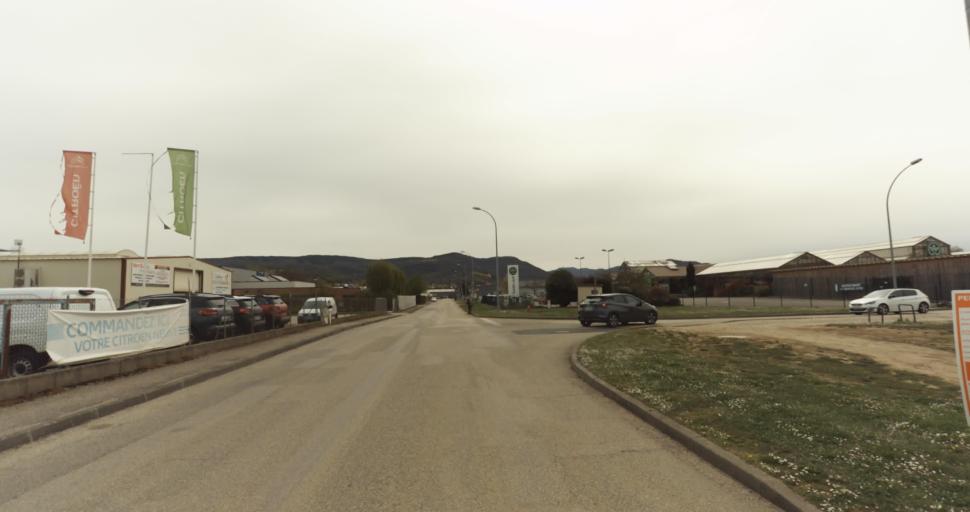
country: FR
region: Rhone-Alpes
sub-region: Departement de l'Ain
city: Amberieu-en-Bugey
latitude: 45.9668
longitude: 5.3410
